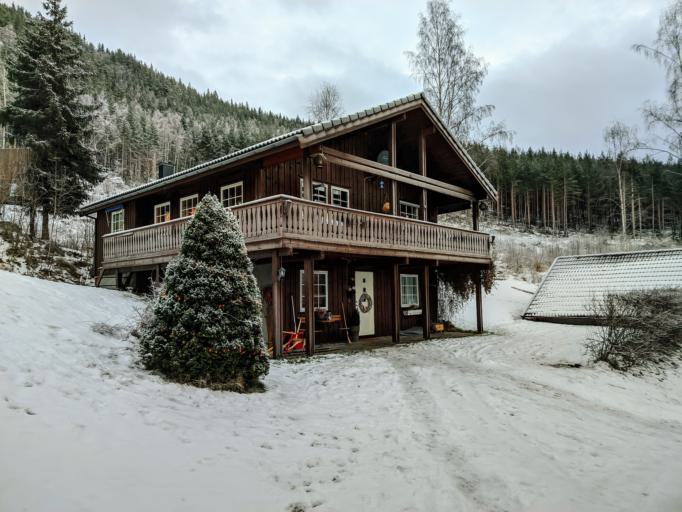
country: NO
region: Oppland
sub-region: Sel
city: Otta
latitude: 61.6839
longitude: 9.5231
